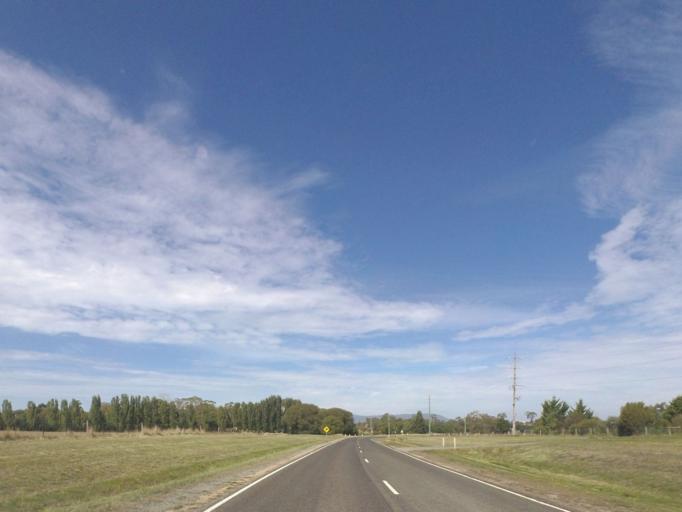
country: AU
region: Victoria
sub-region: Mount Alexander
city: Castlemaine
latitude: -37.2624
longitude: 144.4850
